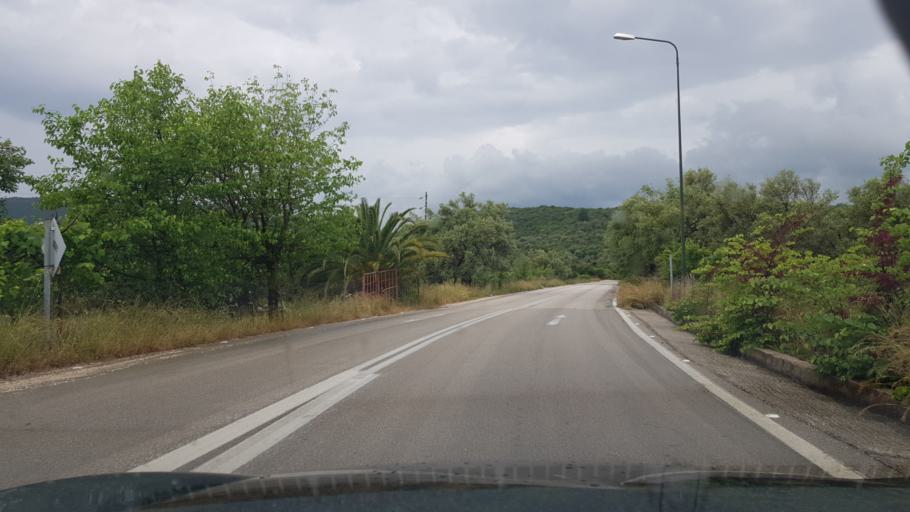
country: GR
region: Ionian Islands
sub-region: Lefkada
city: Nidri
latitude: 38.6493
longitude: 20.6810
